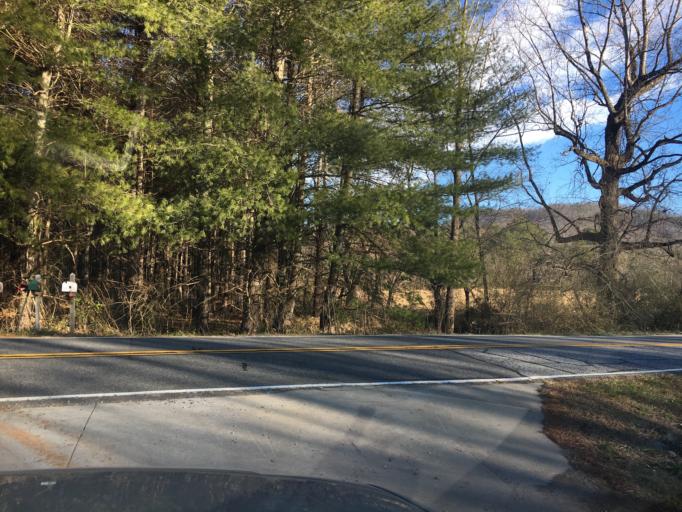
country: US
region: North Carolina
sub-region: McDowell County
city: West Marion
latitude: 35.5978
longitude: -81.9788
